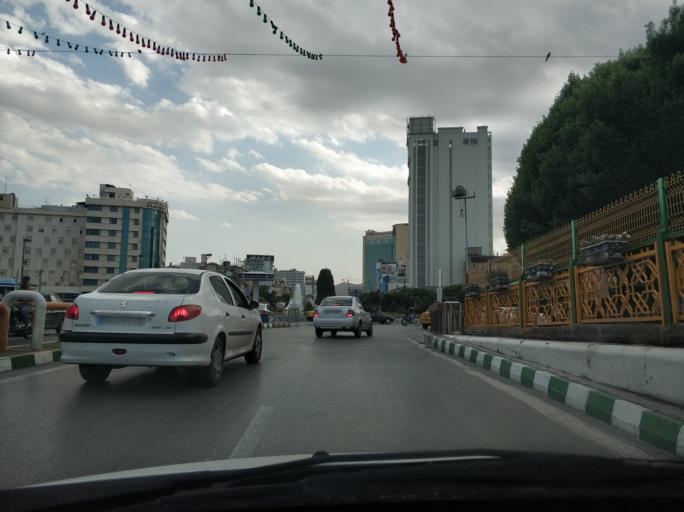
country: IR
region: Razavi Khorasan
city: Mashhad
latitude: 36.2845
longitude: 59.6126
